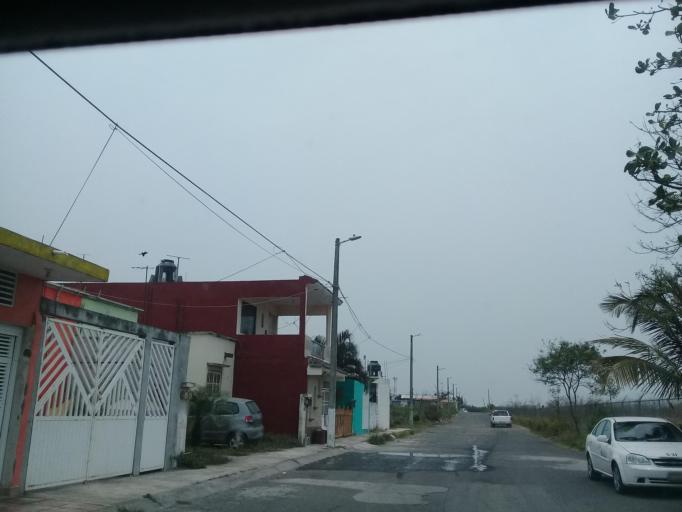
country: MX
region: Veracruz
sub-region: Veracruz
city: Las Amapolas
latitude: 19.1514
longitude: -96.2146
